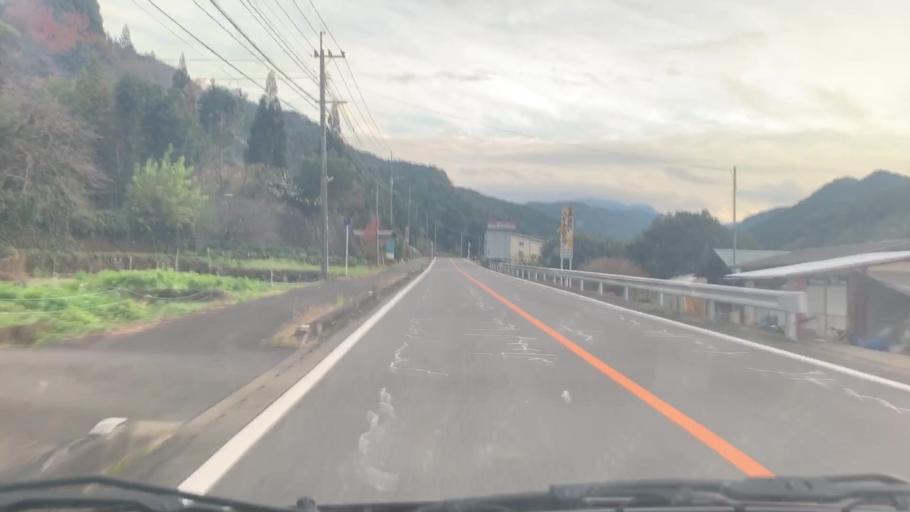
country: JP
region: Saga Prefecture
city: Kashima
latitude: 33.0712
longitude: 130.0693
